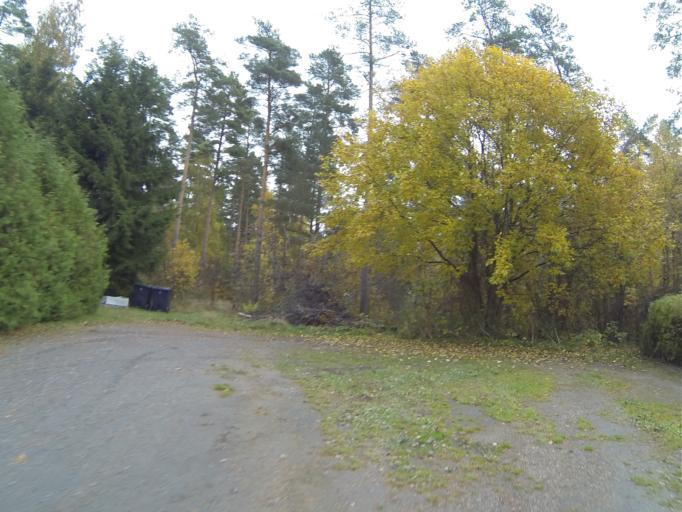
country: SE
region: Skane
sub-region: Sjobo Kommun
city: Blentarp
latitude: 55.6338
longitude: 13.6384
